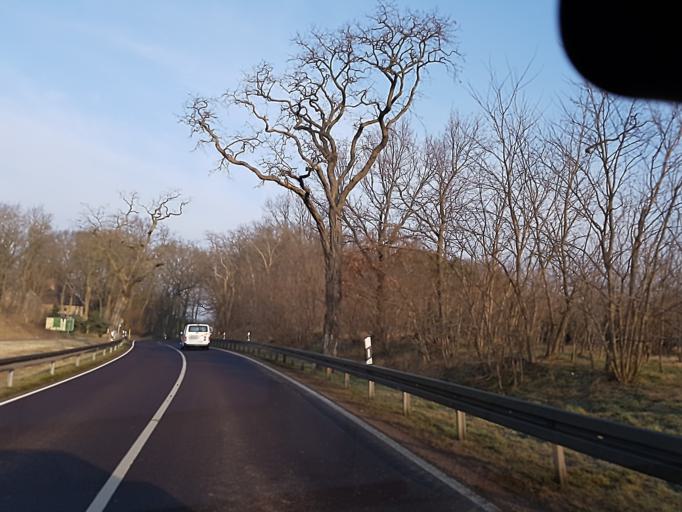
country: DE
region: Brandenburg
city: Gorzke
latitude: 52.1634
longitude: 12.3828
